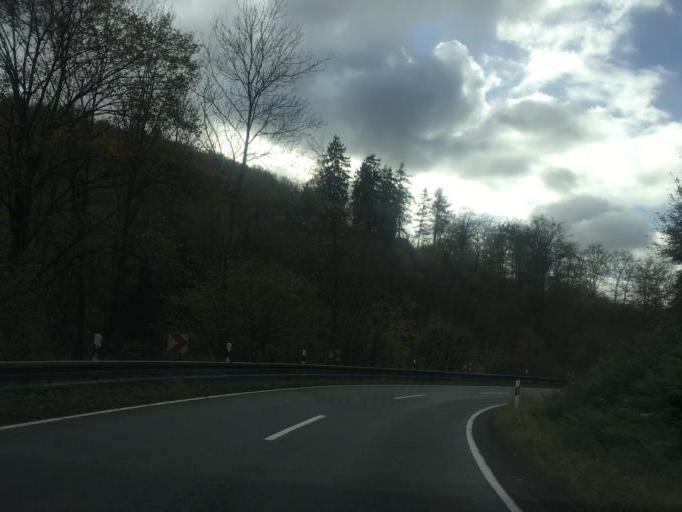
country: DE
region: Lower Saxony
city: Furstenberg
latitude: 51.7441
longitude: 9.4290
